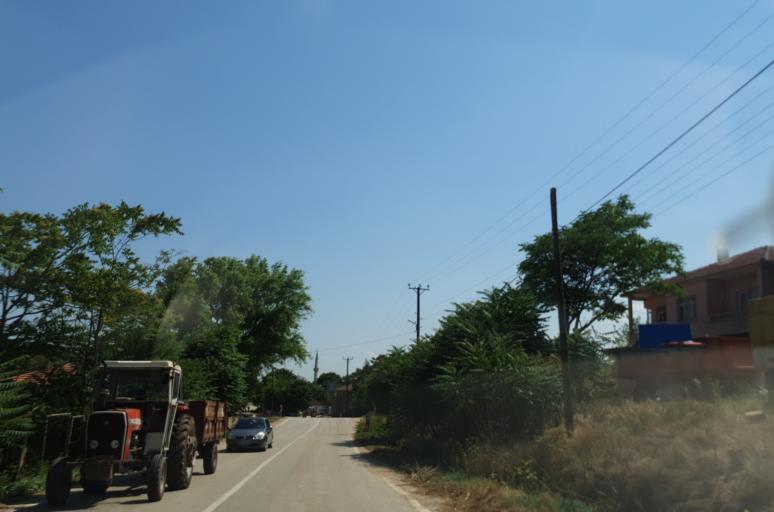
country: TR
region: Kirklareli
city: Vize
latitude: 41.4906
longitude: 27.6943
